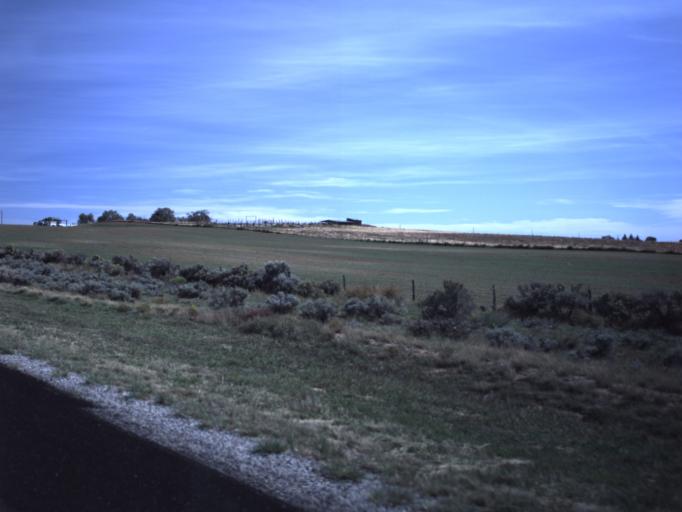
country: US
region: Utah
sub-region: San Juan County
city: Monticello
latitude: 37.8528
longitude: -109.1763
